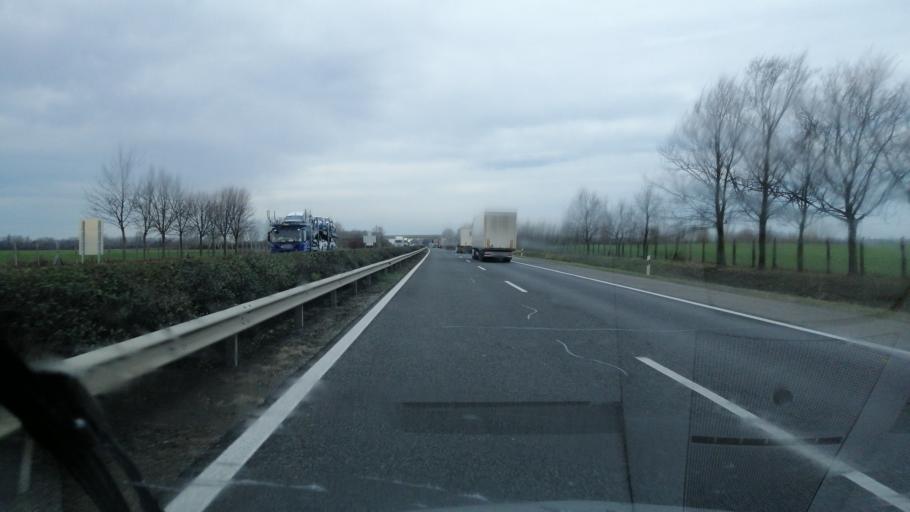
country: HU
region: Gyor-Moson-Sopron
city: Lebeny
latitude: 47.7585
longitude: 17.4024
